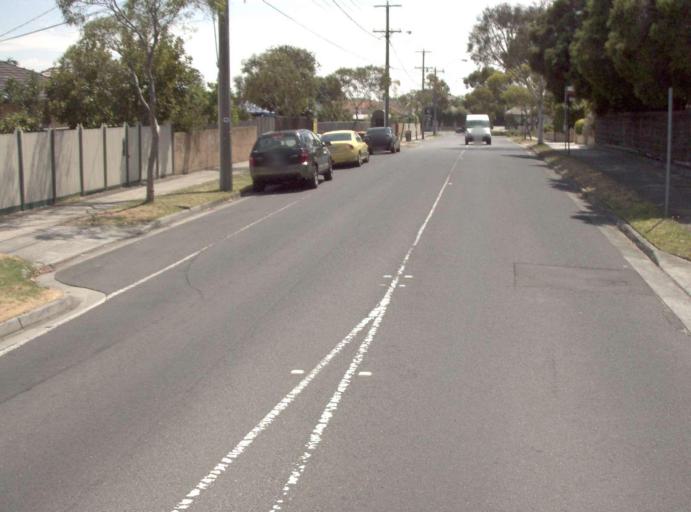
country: AU
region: Victoria
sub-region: Monash
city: Oakleigh South
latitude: -37.9115
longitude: 145.0894
